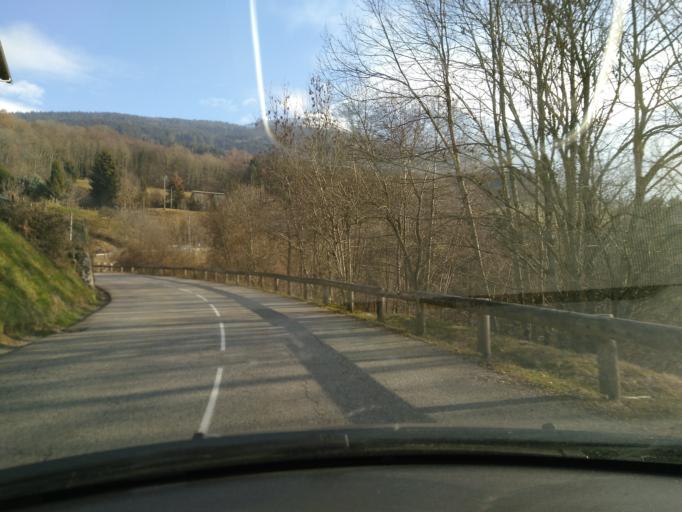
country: FR
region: Rhone-Alpes
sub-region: Departement de l'Isere
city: Villard-Bonnot
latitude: 45.2317
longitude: 5.9320
